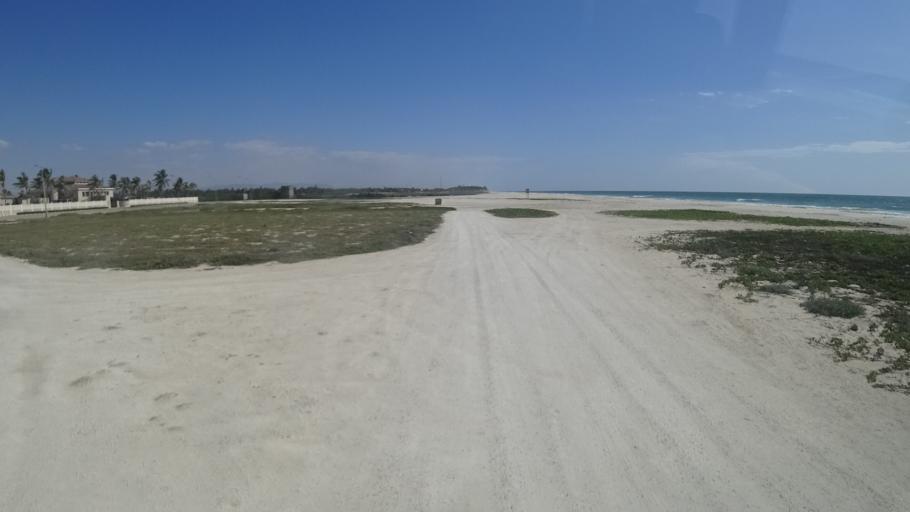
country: OM
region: Zufar
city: Salalah
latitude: 16.9940
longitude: 54.0635
